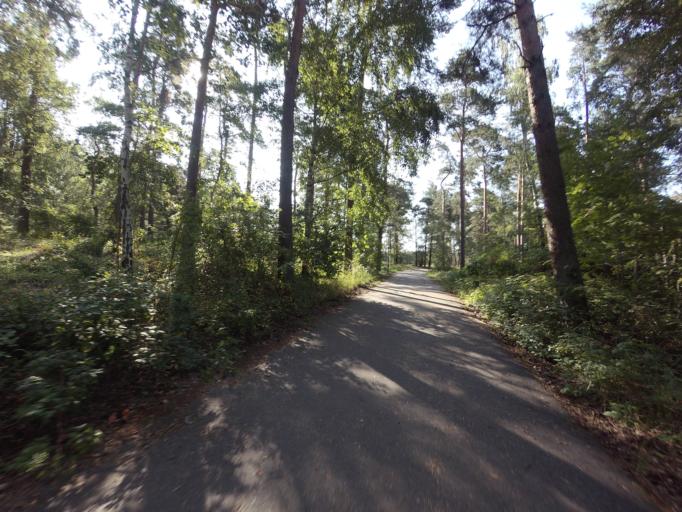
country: SE
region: Skane
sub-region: Kavlinge Kommun
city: Hofterup
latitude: 55.8037
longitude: 12.9773
